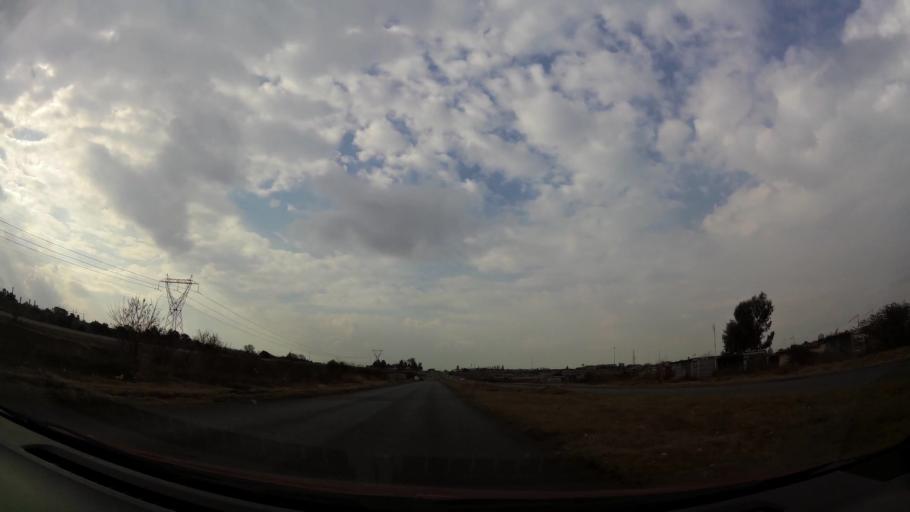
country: ZA
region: Gauteng
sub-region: Sedibeng District Municipality
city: Vanderbijlpark
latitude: -26.6672
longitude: 27.8390
